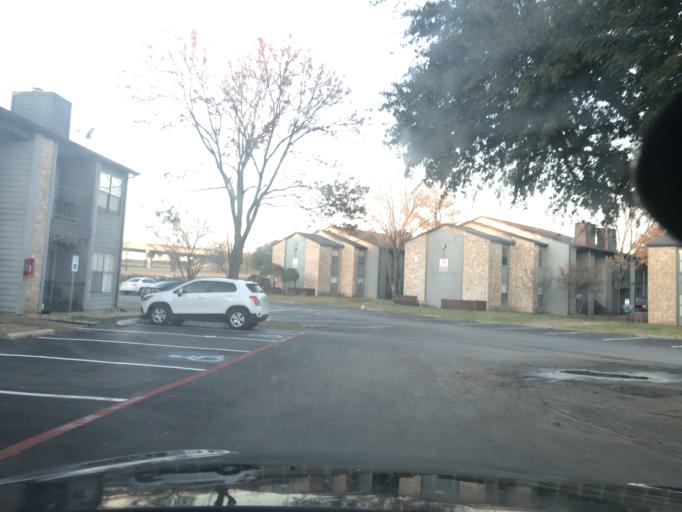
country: US
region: Texas
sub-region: Tarrant County
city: White Settlement
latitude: 32.7357
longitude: -97.4794
